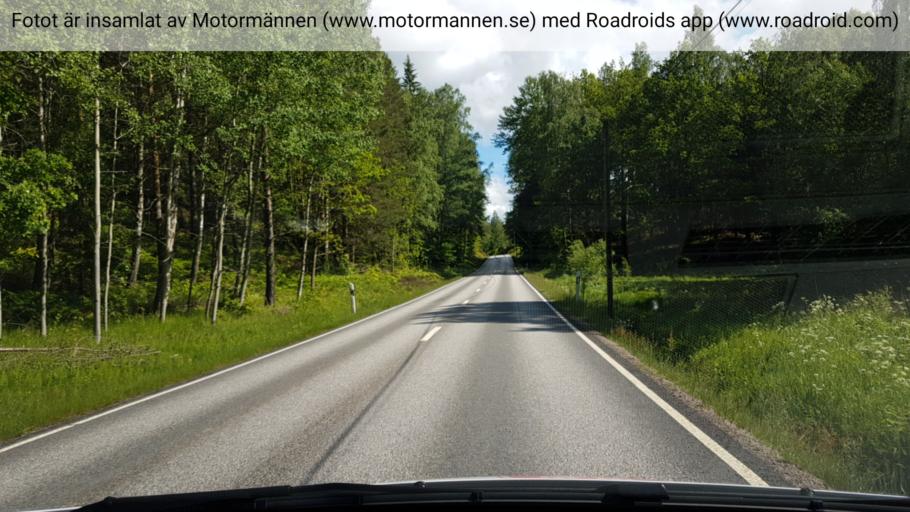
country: SE
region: Kalmar
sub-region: Vasterviks Kommun
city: Overum
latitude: 58.0353
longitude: 16.2297
